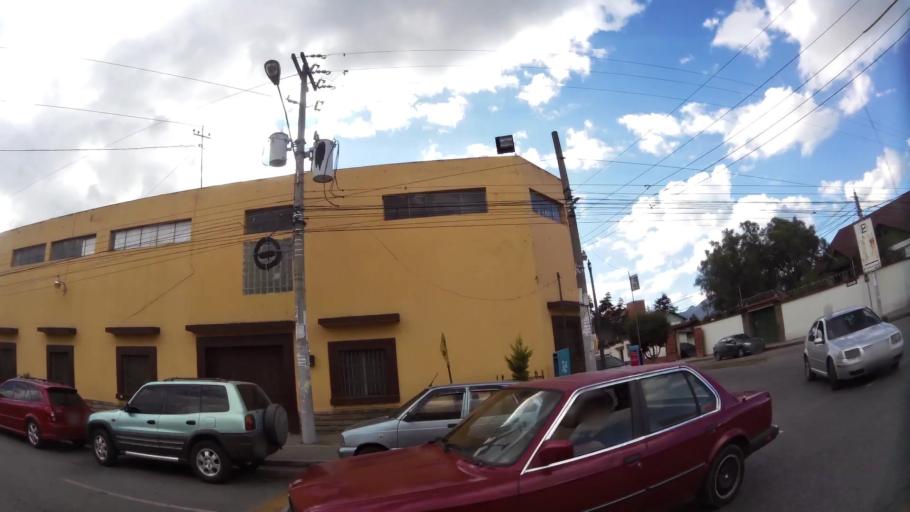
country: GT
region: Quetzaltenango
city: Quetzaltenango
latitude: 14.8427
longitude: -91.5235
